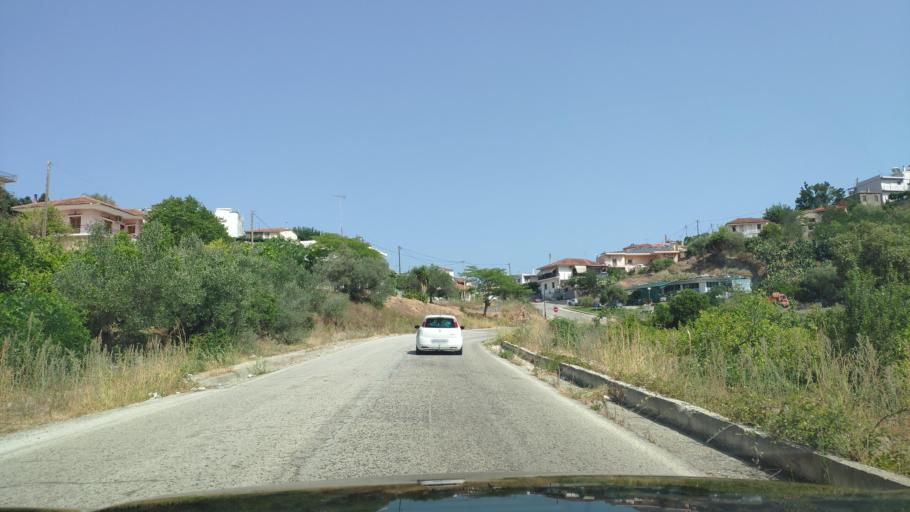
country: GR
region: Epirus
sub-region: Nomos Artas
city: Peta
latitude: 39.1635
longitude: 21.0352
